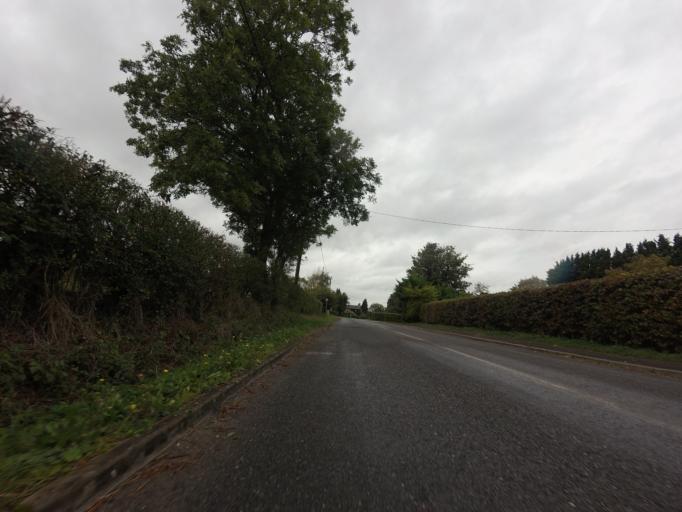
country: GB
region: England
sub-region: Cambridgeshire
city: Comberton
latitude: 52.1570
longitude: 0.0041
